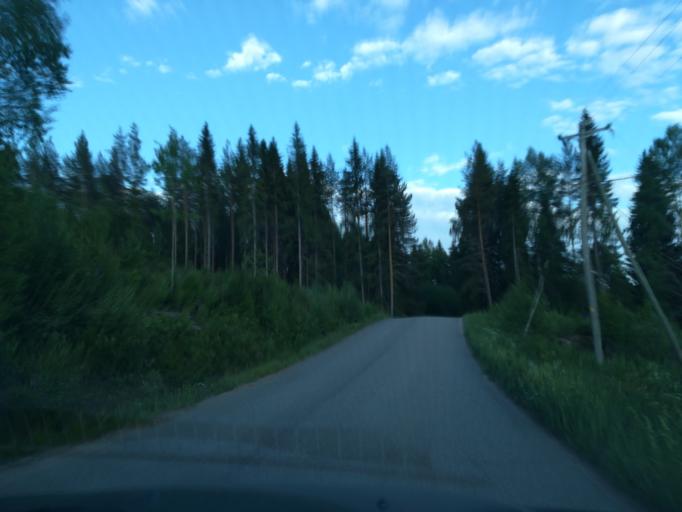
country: FI
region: Southern Savonia
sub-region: Mikkeli
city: Puumala
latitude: 61.5764
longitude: 28.1405
